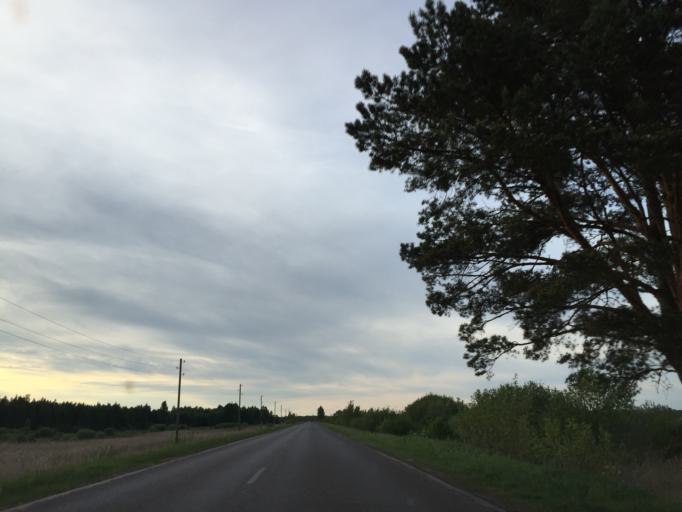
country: LV
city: Tireli
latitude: 56.8200
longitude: 23.5701
